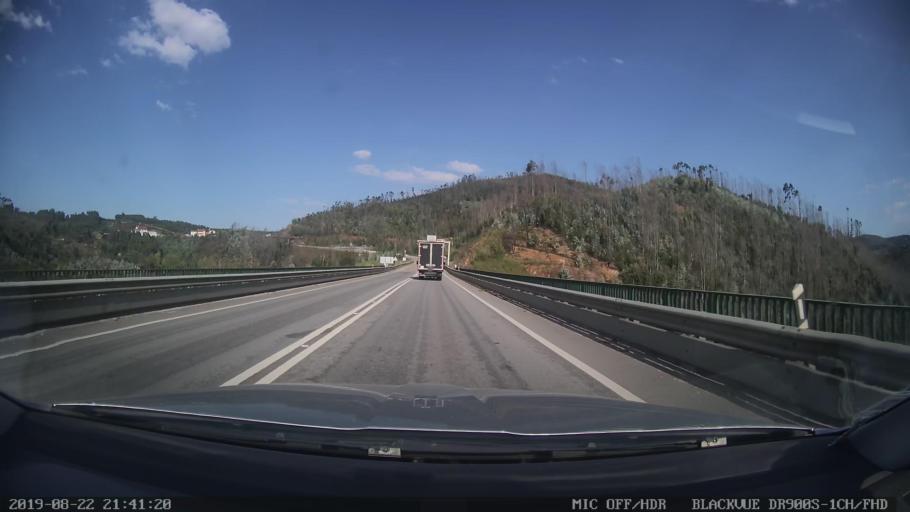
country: PT
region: Leiria
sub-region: Figueiro Dos Vinhos
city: Figueiro dos Vinhos
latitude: 39.9267
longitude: -8.3237
